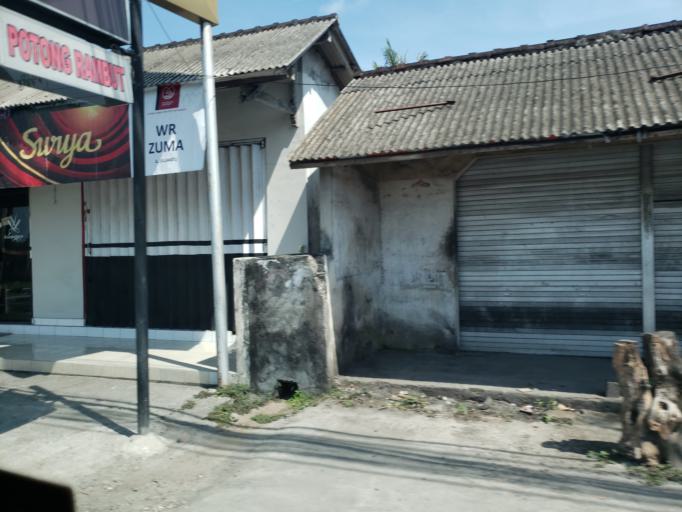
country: ID
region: Bali
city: Kangin
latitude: -8.8233
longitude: 115.1426
